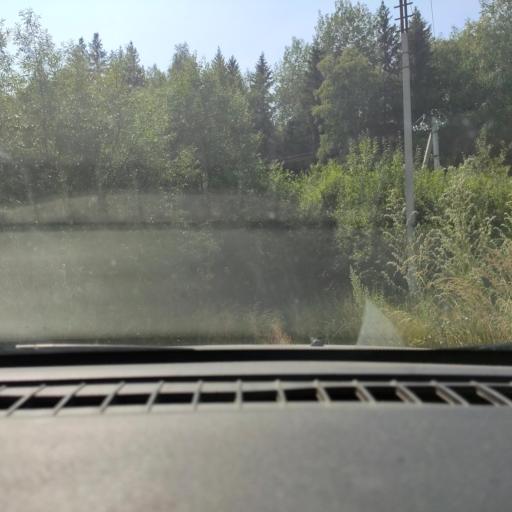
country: RU
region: Perm
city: Novyye Lyady
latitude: 58.1261
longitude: 56.4686
